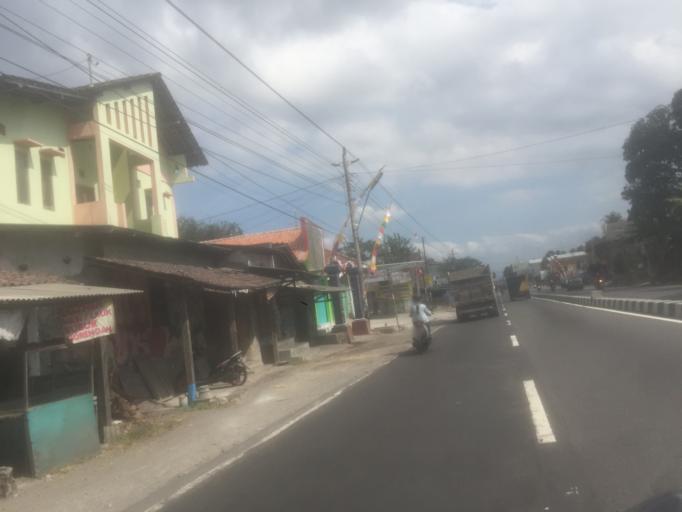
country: ID
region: Central Java
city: Muntilan
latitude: -7.6157
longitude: 110.3080
